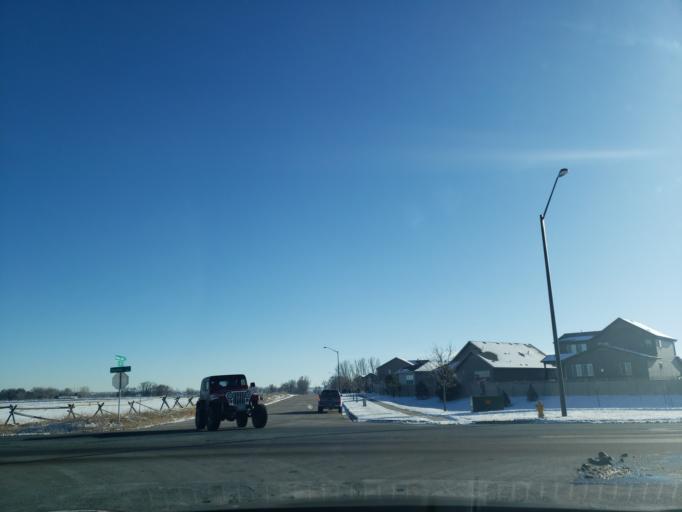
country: US
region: Colorado
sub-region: Weld County
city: Windsor
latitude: 40.5088
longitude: -105.0008
